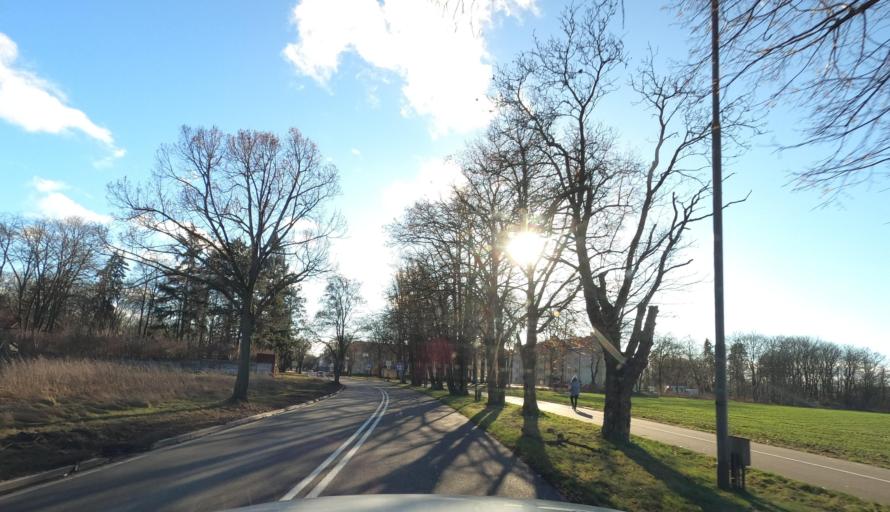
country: PL
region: West Pomeranian Voivodeship
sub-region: Powiat pyrzycki
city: Warnice
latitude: 53.2965
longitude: 14.9934
